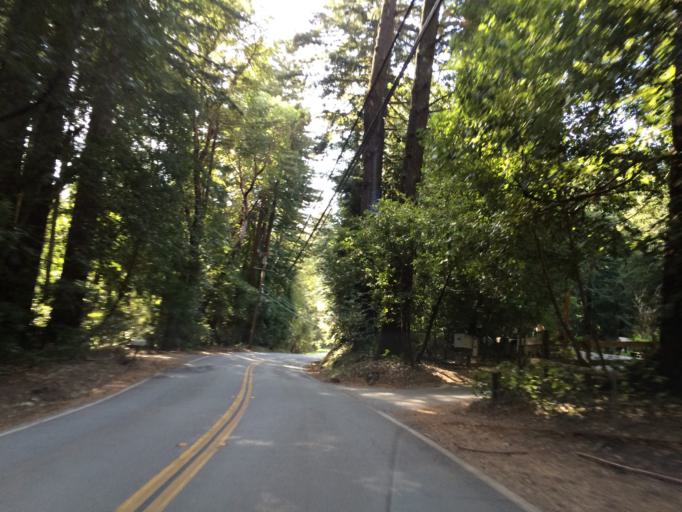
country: US
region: California
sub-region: Santa Cruz County
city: Brookdale
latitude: 37.0856
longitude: -122.1360
